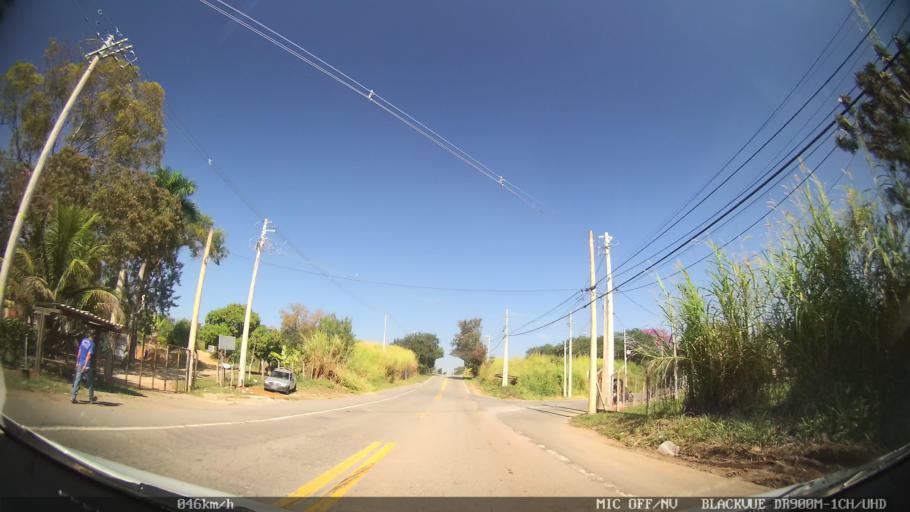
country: BR
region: Sao Paulo
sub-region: Campinas
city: Campinas
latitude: -22.9874
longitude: -47.0855
